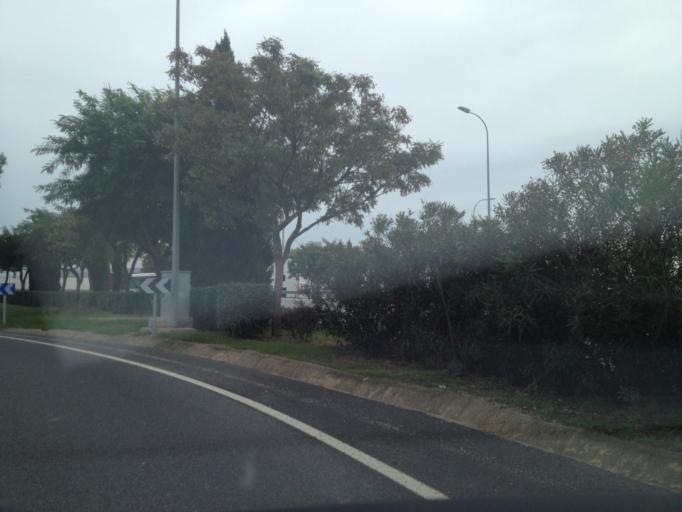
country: ES
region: Balearic Islands
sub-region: Illes Balears
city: s'Arenal
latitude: 39.5442
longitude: 2.7268
